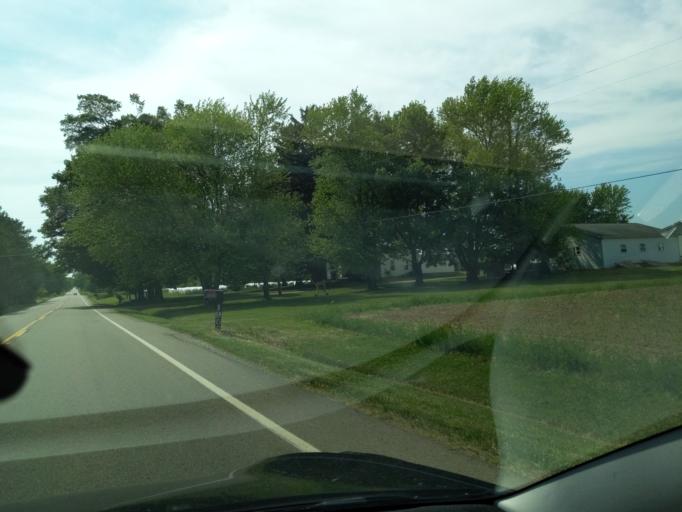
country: US
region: Michigan
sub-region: Eaton County
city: Grand Ledge
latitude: 42.7120
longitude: -84.7993
